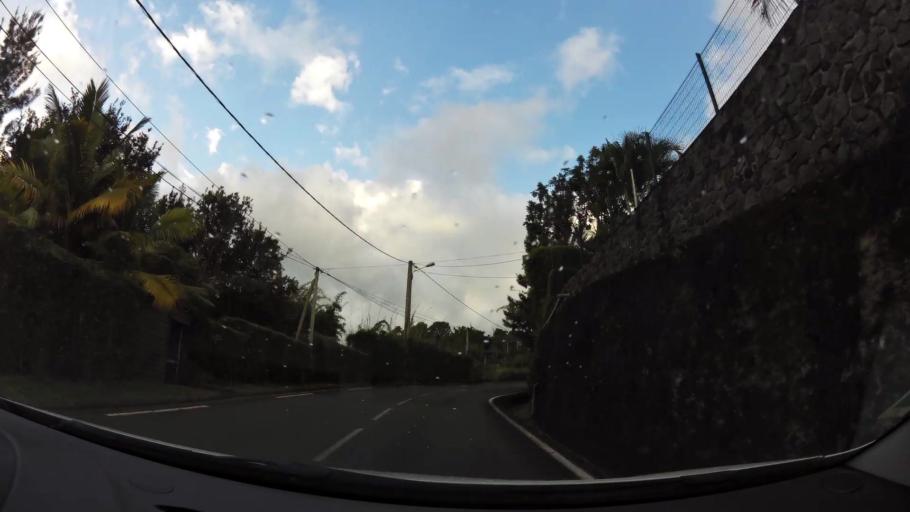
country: RE
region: Reunion
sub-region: Reunion
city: Saint-Denis
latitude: -20.9138
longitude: 55.4396
